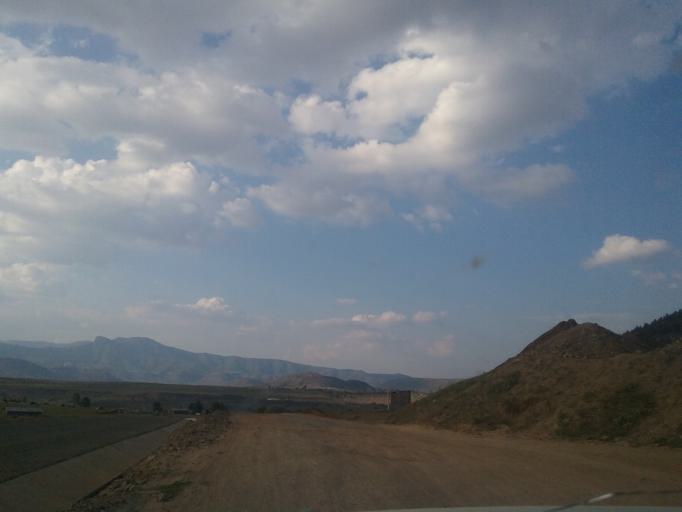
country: LS
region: Quthing
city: Quthing
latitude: -30.4024
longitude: 27.6102
